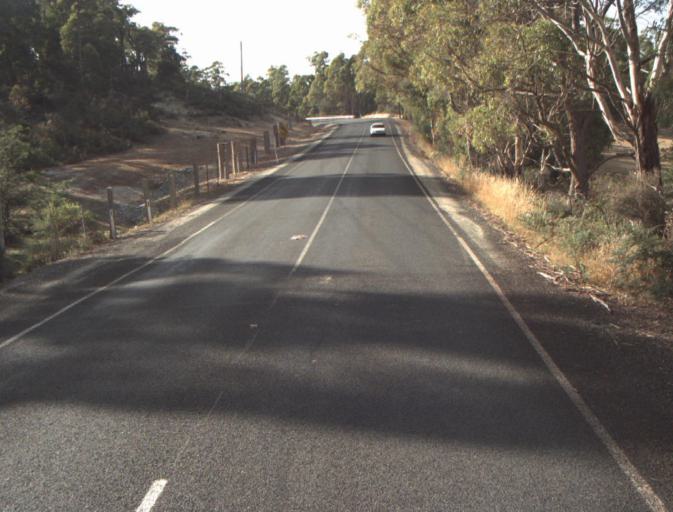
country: AU
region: Tasmania
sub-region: Dorset
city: Bridport
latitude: -41.1650
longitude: 147.2511
